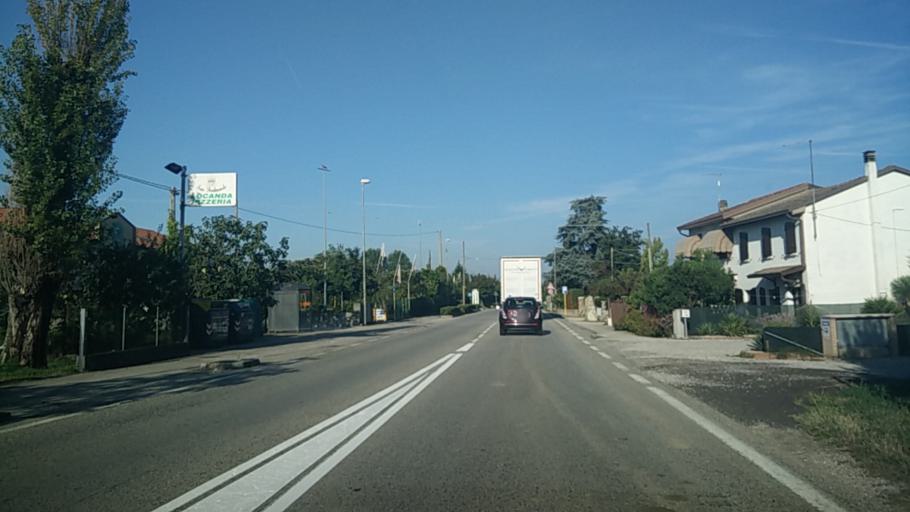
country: IT
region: Veneto
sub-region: Provincia di Venezia
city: Scorze
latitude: 45.5763
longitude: 12.0972
